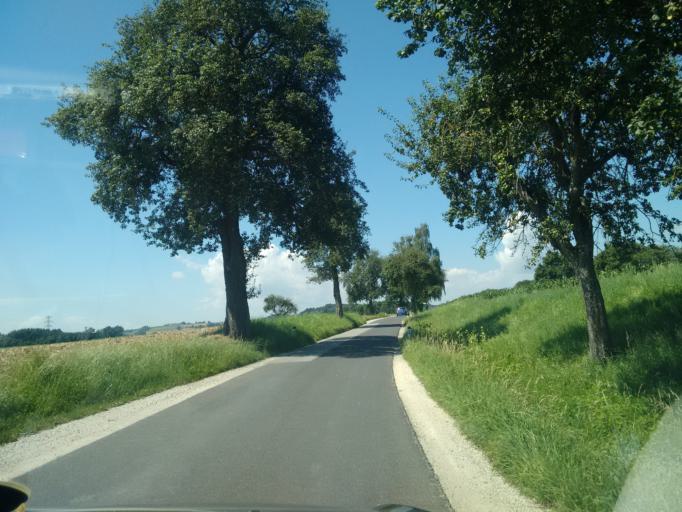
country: AT
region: Upper Austria
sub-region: Wels-Land
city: Gunskirchen
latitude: 48.1759
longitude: 13.9666
